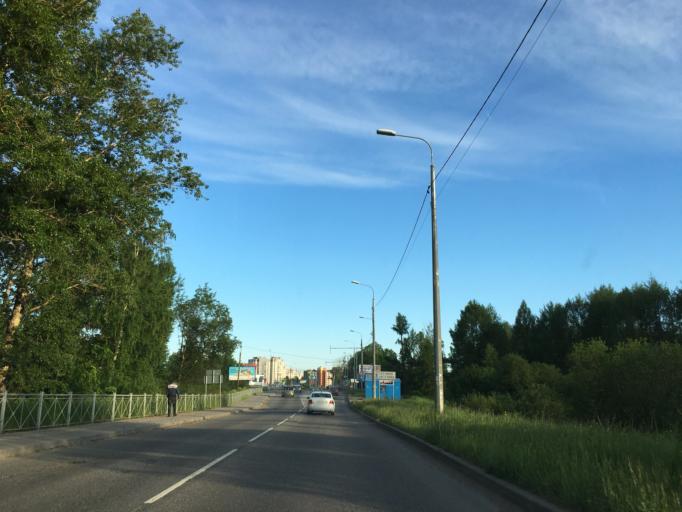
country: RU
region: Leningrad
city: Gatchina
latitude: 59.5869
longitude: 30.1359
